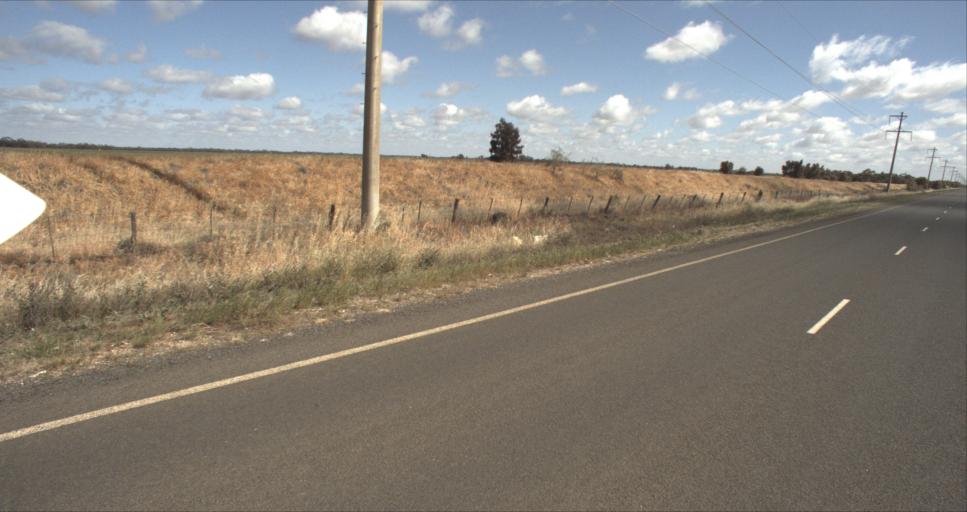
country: AU
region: New South Wales
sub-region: Murrumbidgee Shire
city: Darlington Point
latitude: -34.5379
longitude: 146.1727
